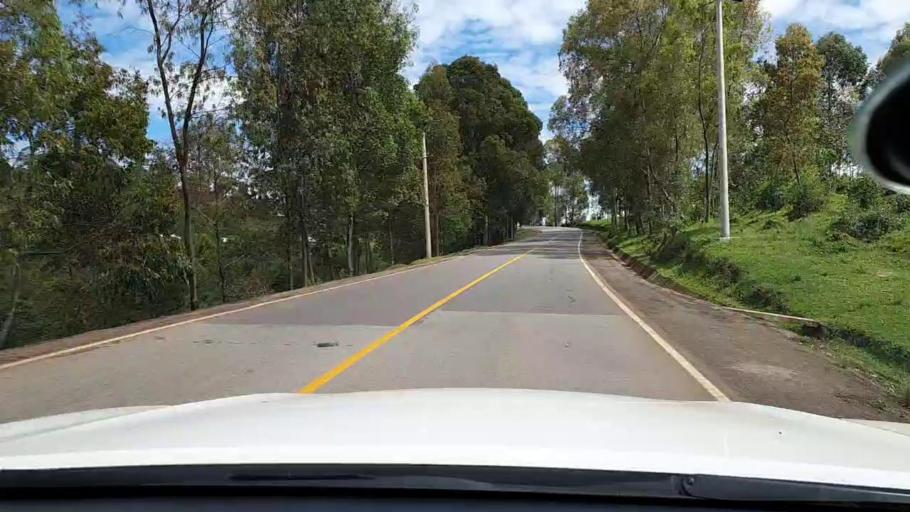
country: RW
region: Kigali
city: Kigali
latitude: -1.8187
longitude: 29.9409
